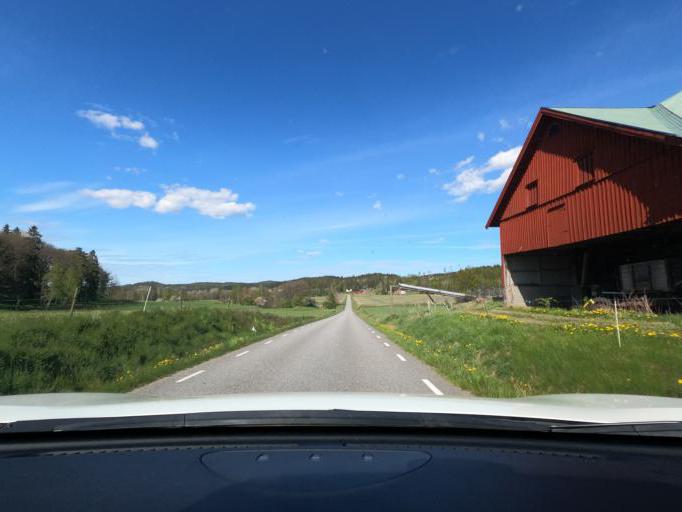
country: SE
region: Vaestra Goetaland
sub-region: Harryda Kommun
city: Ravlanda
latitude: 57.6107
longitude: 12.4872
